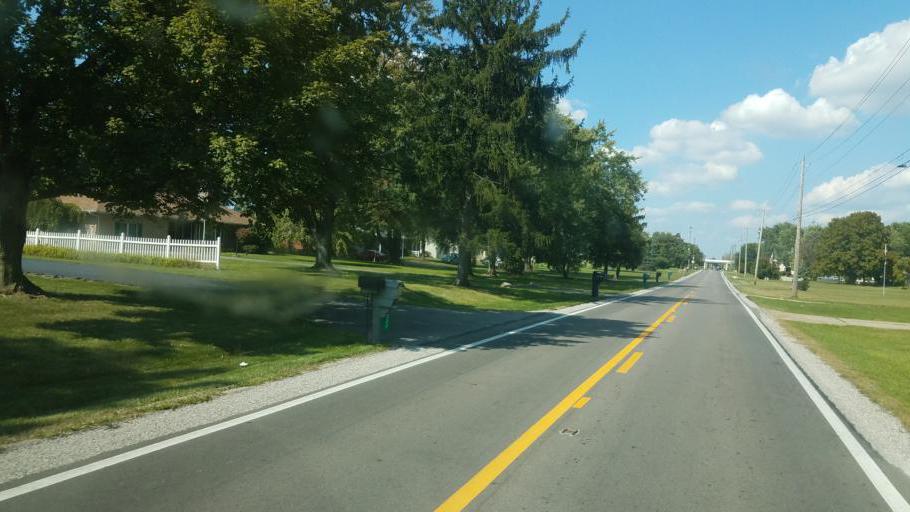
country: US
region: Ohio
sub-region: Franklin County
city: Grove City
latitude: 39.9071
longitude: -83.1082
